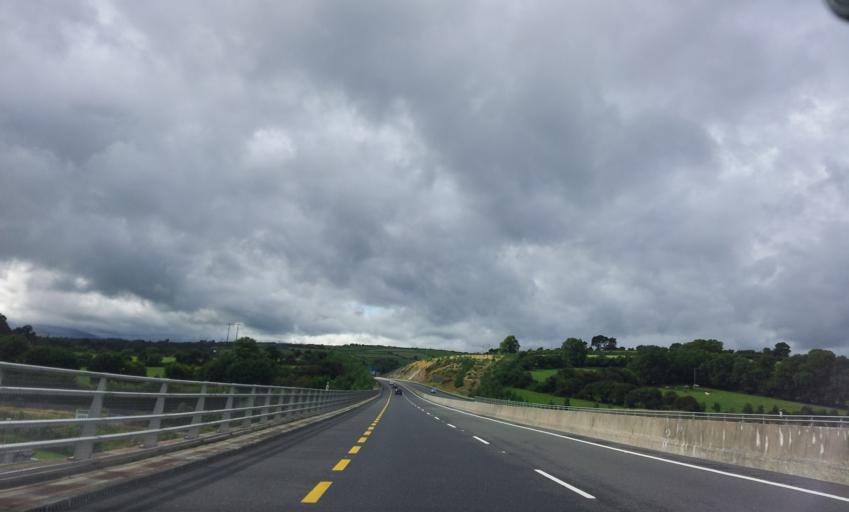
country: IE
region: Leinster
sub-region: Kilkenny
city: Mooncoin
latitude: 52.2379
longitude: -7.2369
